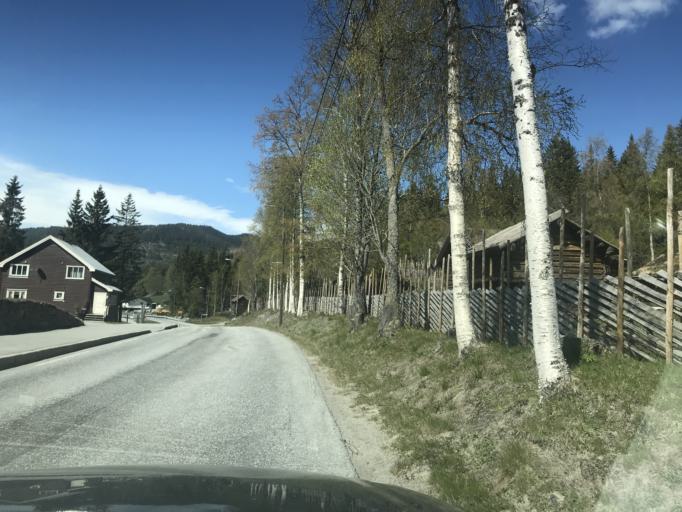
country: NO
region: Telemark
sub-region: Hjartdal
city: Sauland
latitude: 59.7538
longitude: 8.7962
